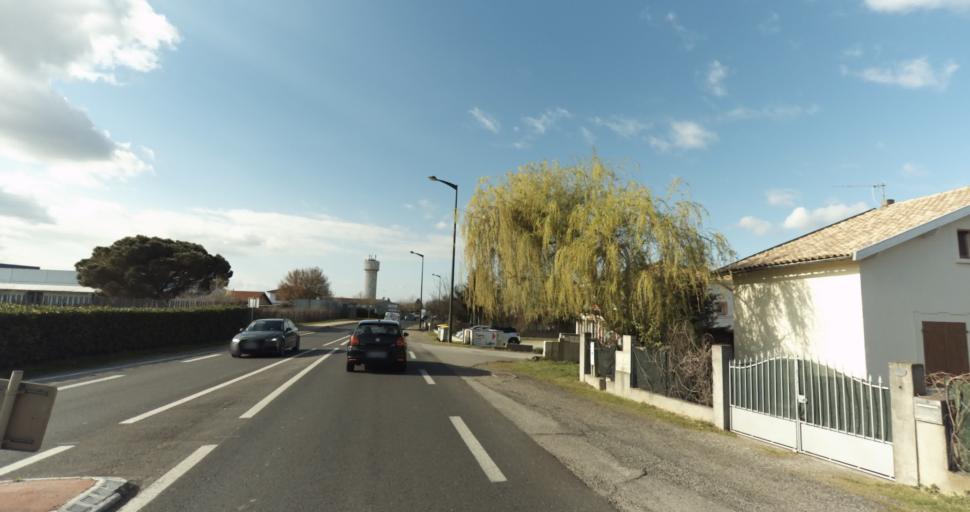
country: FR
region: Midi-Pyrenees
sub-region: Departement de la Haute-Garonne
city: Auterive
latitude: 43.3574
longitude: 1.4665
